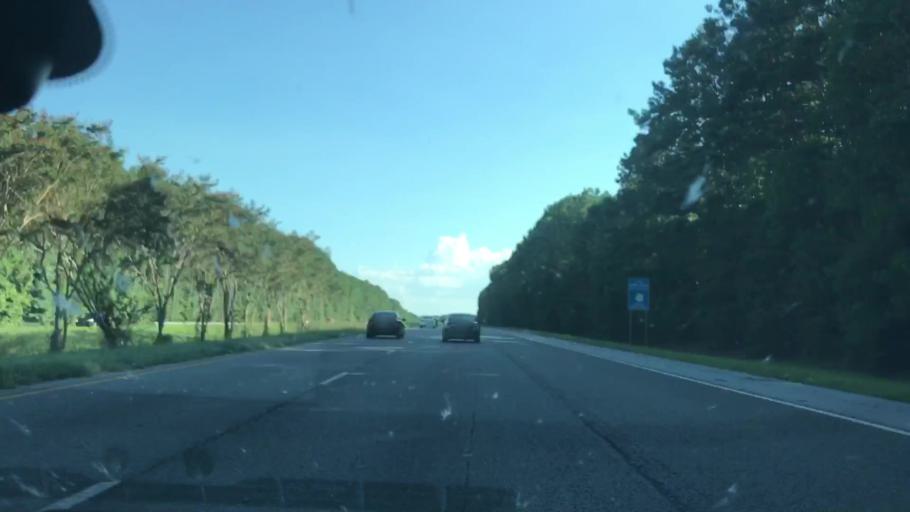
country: US
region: Georgia
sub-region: Harris County
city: Hamilton
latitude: 32.8085
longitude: -85.0214
